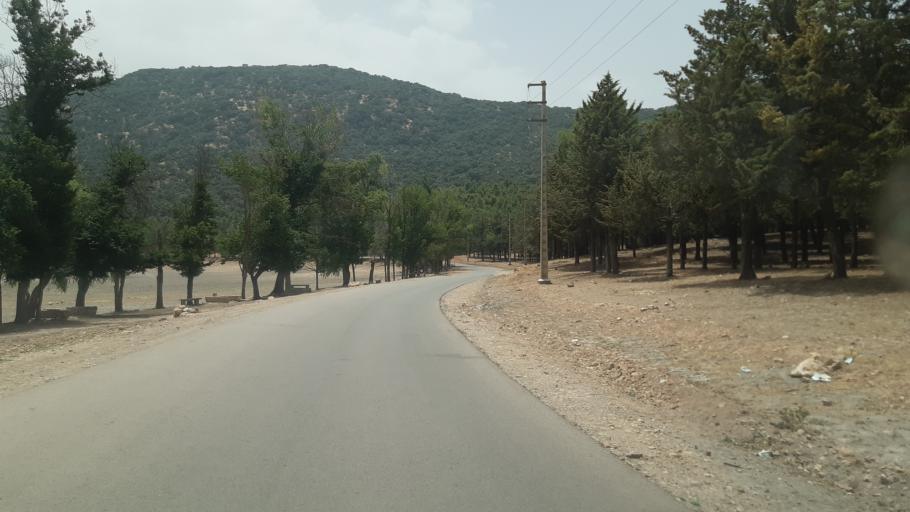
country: MA
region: Meknes-Tafilalet
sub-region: Ifrane
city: Ifrane
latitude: 33.6576
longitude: -5.0433
